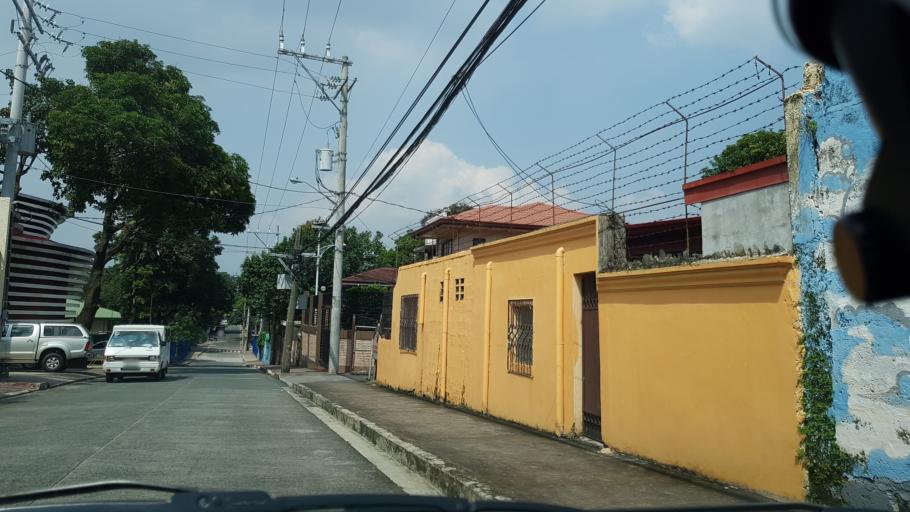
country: PH
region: Calabarzon
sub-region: Province of Rizal
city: Antipolo
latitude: 14.6478
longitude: 121.1185
